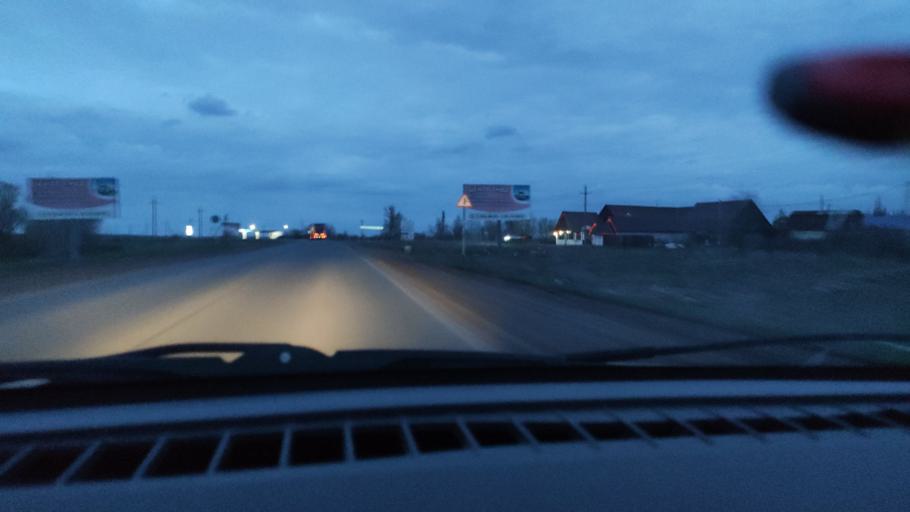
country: RU
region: Orenburg
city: Tatarskaya Kargala
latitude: 51.9029
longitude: 55.1690
